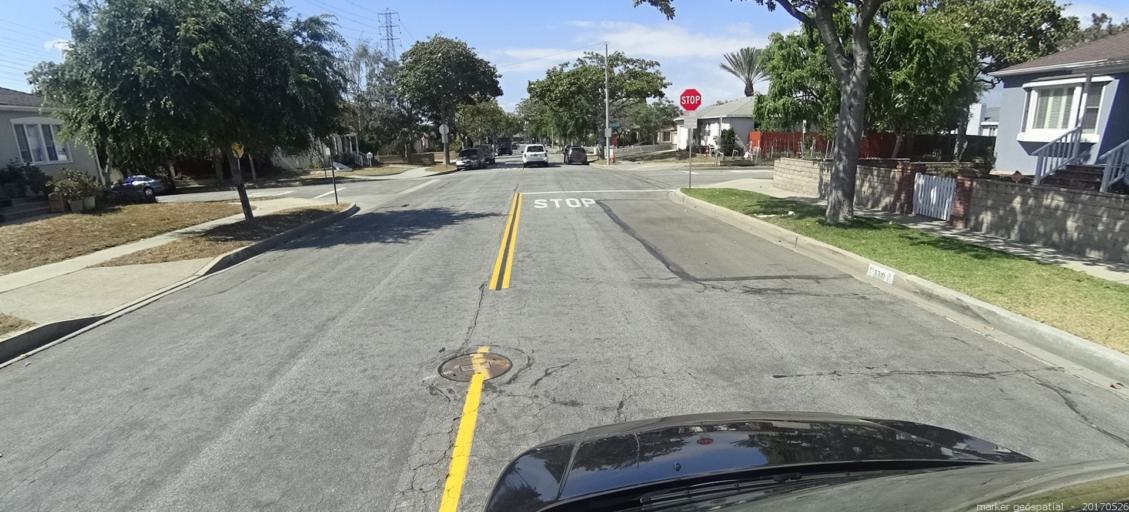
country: US
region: California
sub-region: Los Angeles County
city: Lawndale
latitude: 33.8851
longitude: -118.3651
